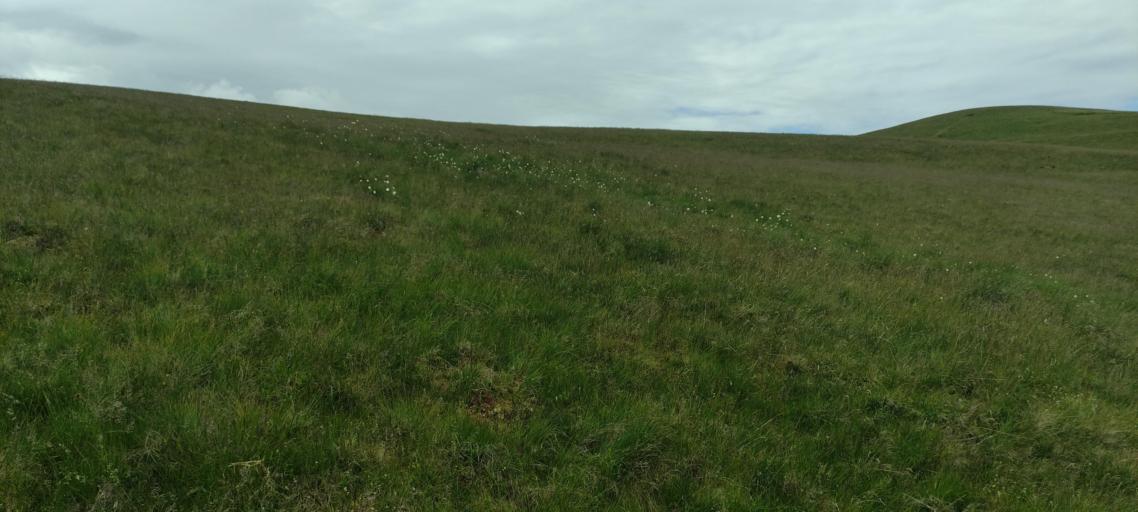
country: GB
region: England
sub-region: Cumbria
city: Keswick
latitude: 54.7031
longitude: -3.1171
